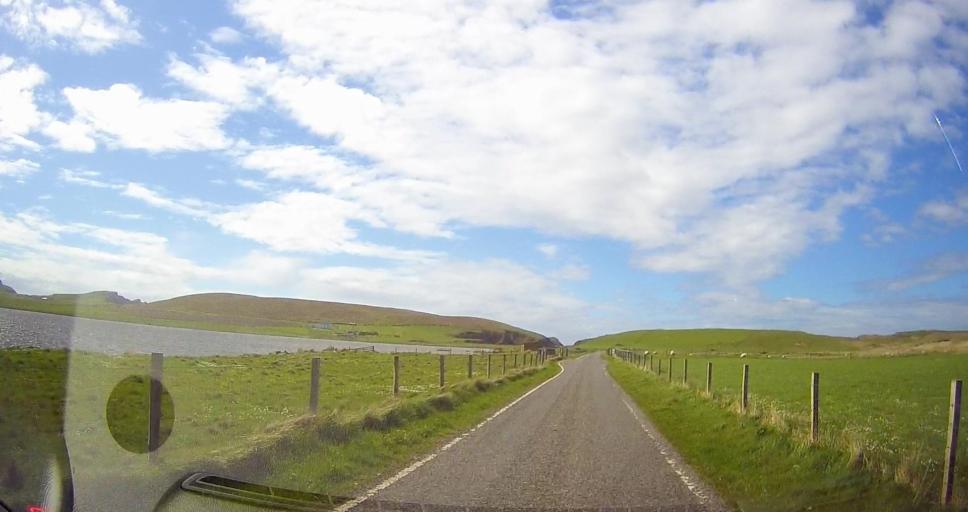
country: GB
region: Scotland
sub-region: Shetland Islands
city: Sandwick
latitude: 59.9420
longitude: -1.3343
